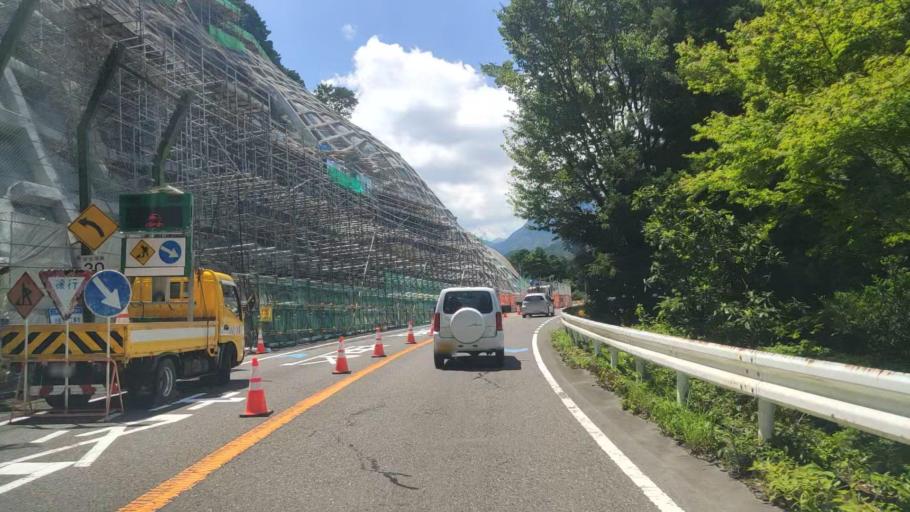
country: JP
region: Mie
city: Owase
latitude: 34.1025
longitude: 136.2004
